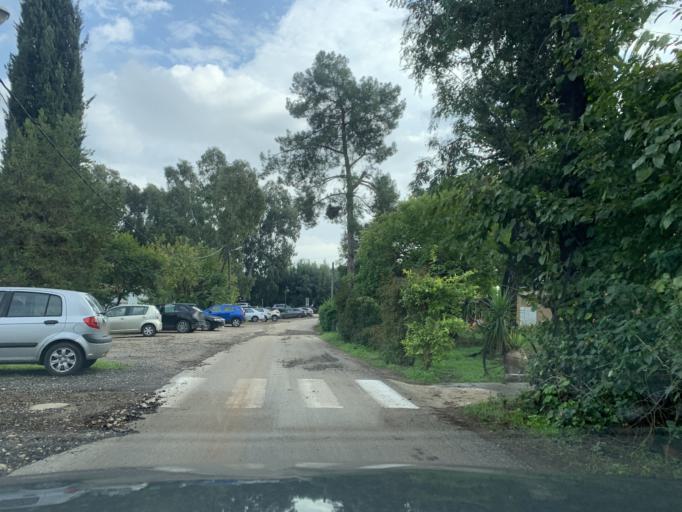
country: PS
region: West Bank
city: Qalqilyah
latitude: 32.1962
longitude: 34.9473
